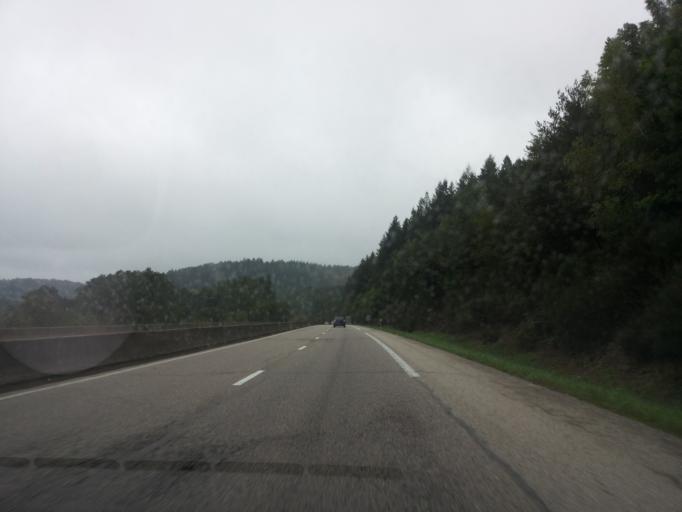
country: FR
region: Lorraine
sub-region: Departement des Vosges
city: Arches
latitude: 48.1448
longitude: 6.5085
